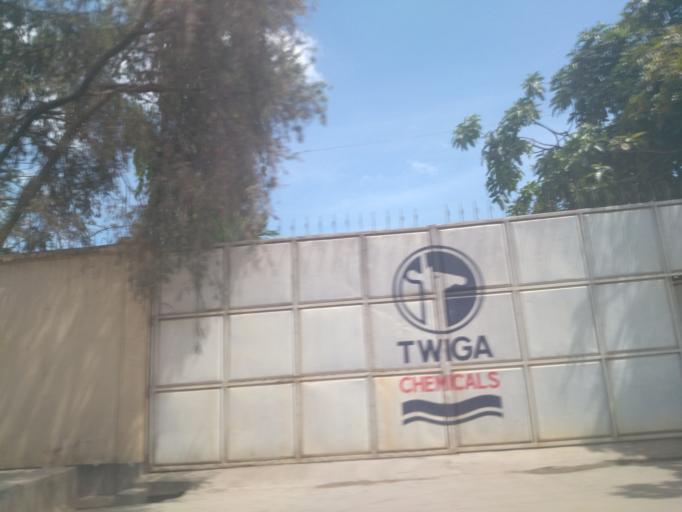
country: TZ
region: Dar es Salaam
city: Dar es Salaam
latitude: -6.8421
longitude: 39.2581
